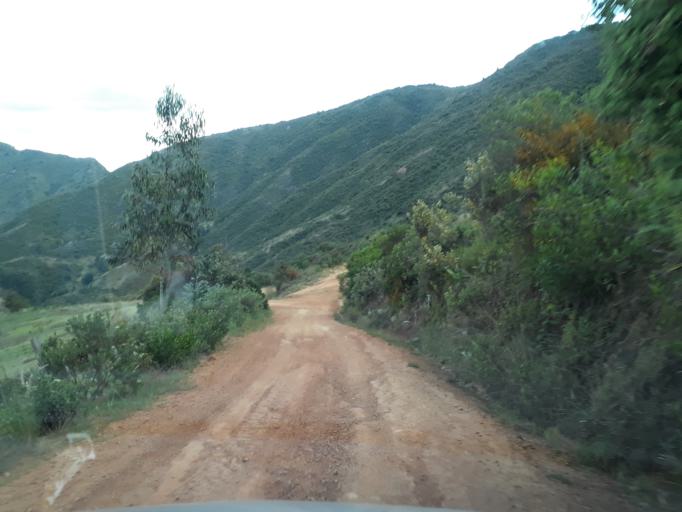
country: CO
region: Boyaca
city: Santa Rosa de Viterbo
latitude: 5.8611
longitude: -72.9689
